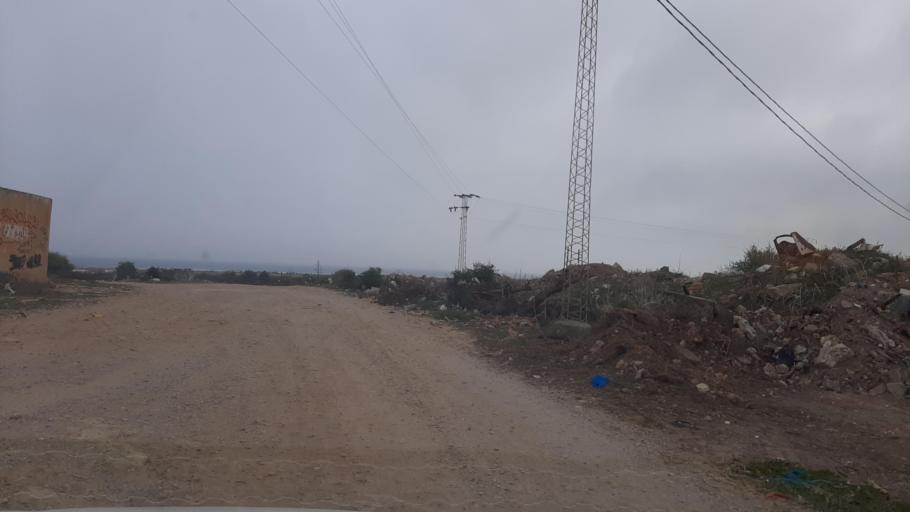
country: TN
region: Nabul
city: Menzel Heurr
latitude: 36.6943
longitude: 10.9355
